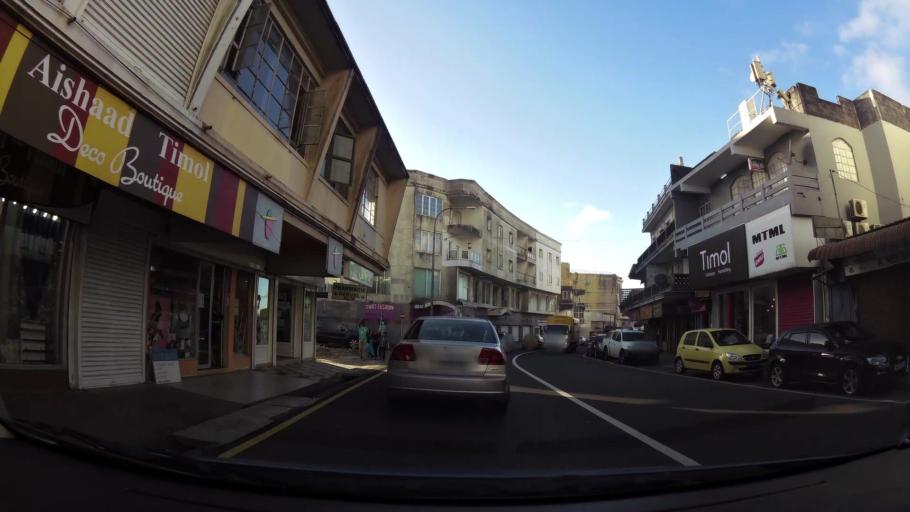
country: MU
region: Plaines Wilhems
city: Curepipe
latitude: -20.3162
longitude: 57.5232
